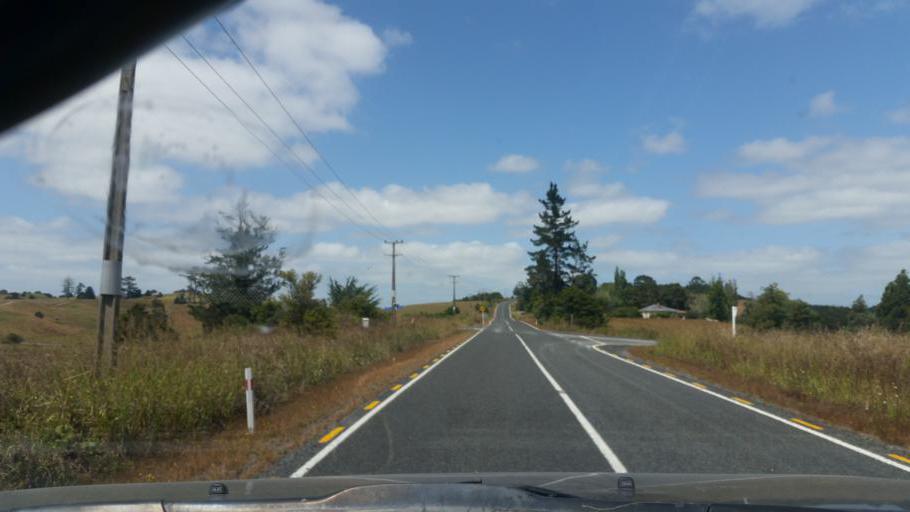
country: NZ
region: Northland
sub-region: Whangarei
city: Ruakaka
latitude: -36.0394
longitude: 174.2796
